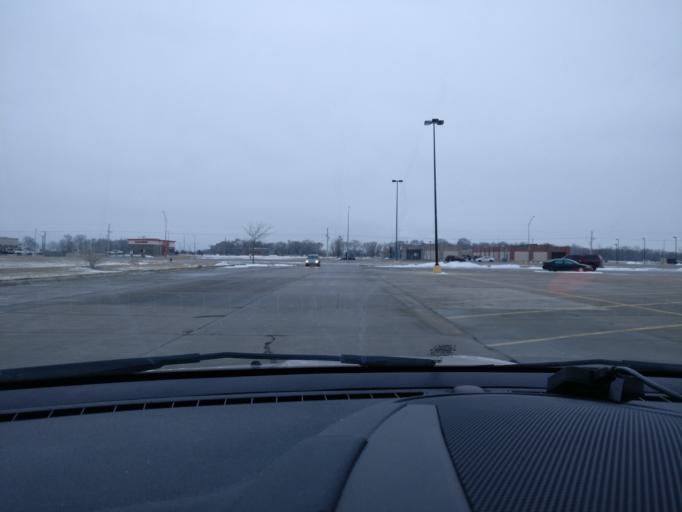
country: US
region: Nebraska
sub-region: Dodge County
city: Fremont
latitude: 41.4524
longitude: -96.4561
